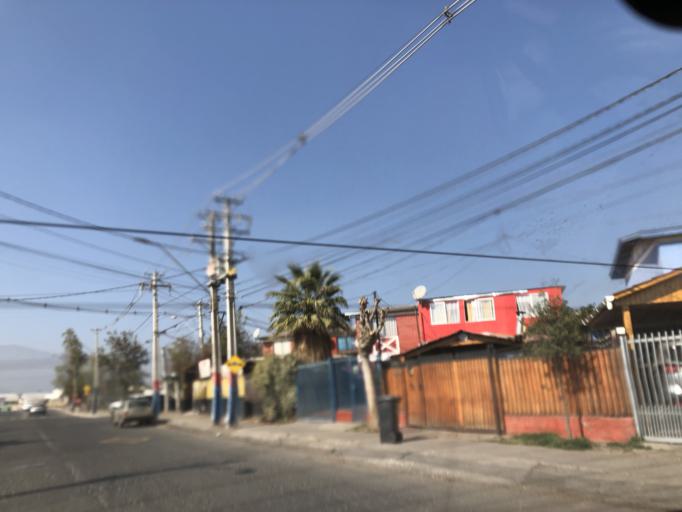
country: CL
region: Santiago Metropolitan
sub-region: Provincia de Cordillera
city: Puente Alto
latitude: -33.6158
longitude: -70.5939
